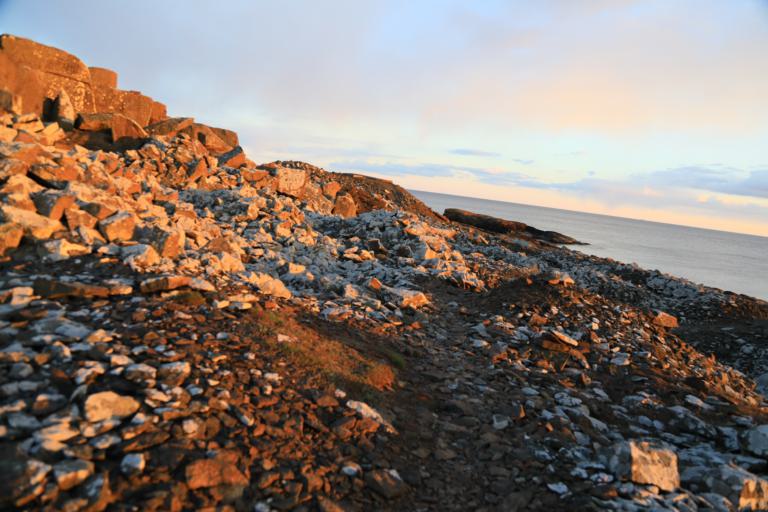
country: SE
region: Halland
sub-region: Varbergs Kommun
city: Varberg
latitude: 57.0879
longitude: 12.2363
